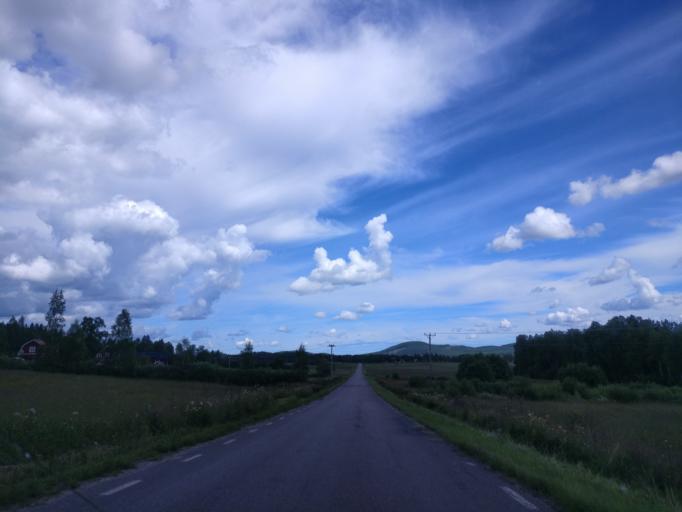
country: SE
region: Vaermland
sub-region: Hagfors Kommun
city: Ekshaerad
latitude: 60.1195
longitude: 13.4517
